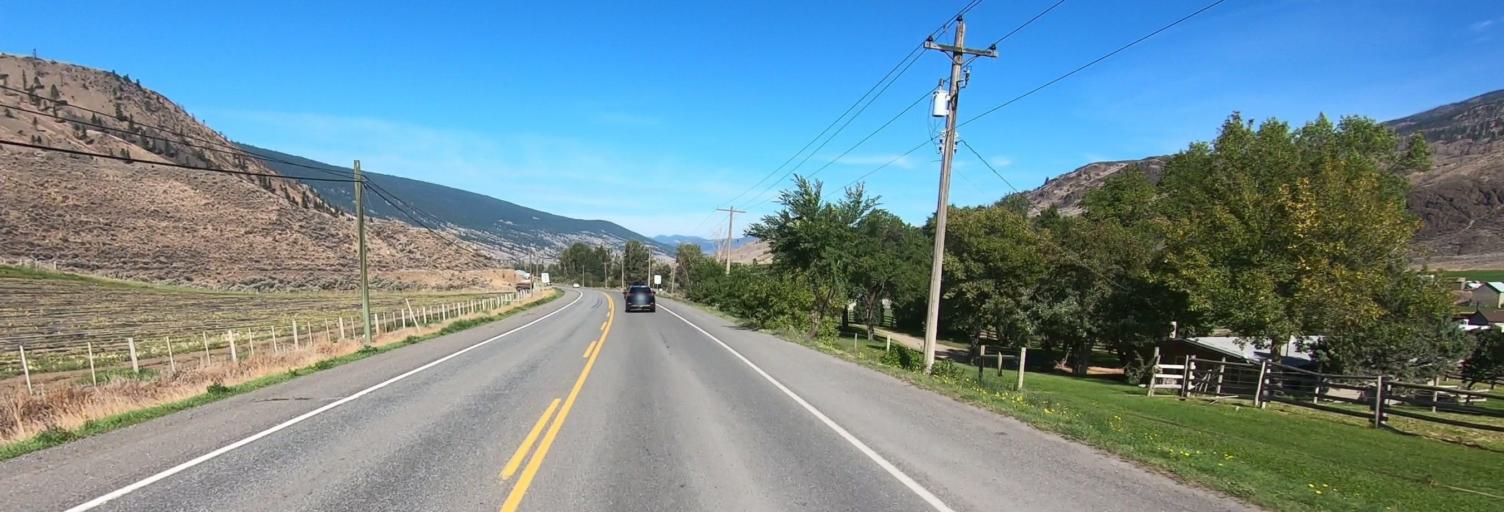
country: CA
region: British Columbia
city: Cache Creek
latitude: 50.8203
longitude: -121.3349
